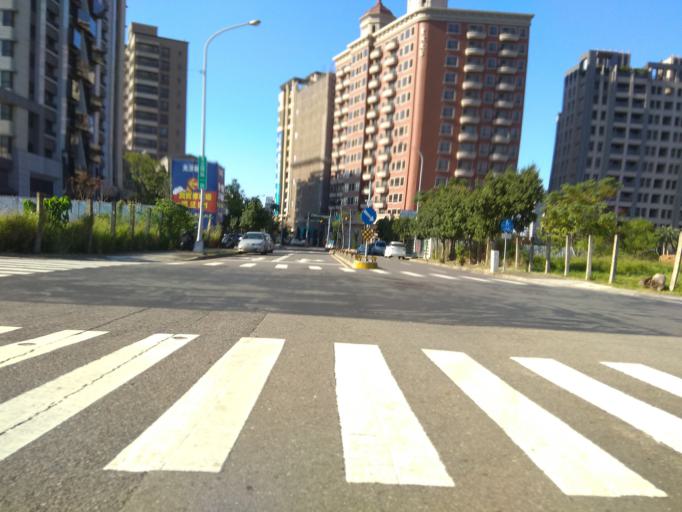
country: TW
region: Taiwan
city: Taoyuan City
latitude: 25.0037
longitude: 121.2118
